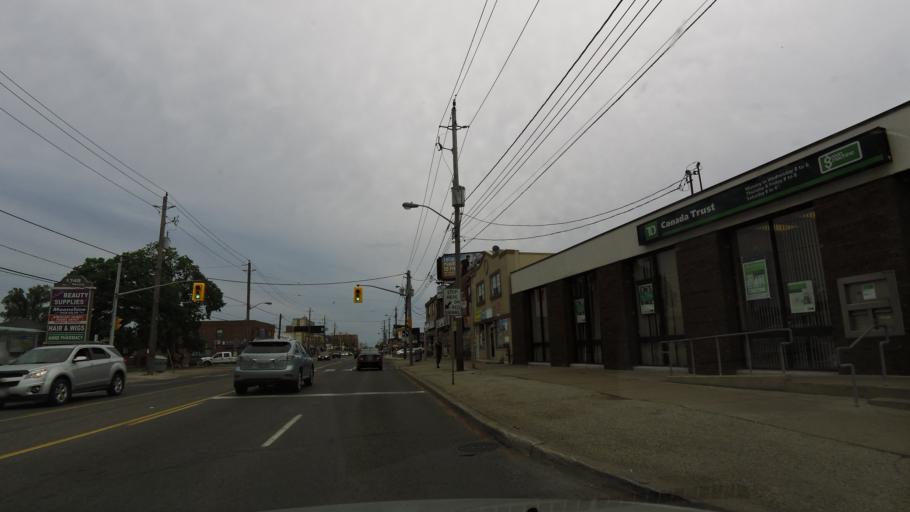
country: CA
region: Ontario
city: Etobicoke
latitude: 43.7051
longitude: -79.5045
